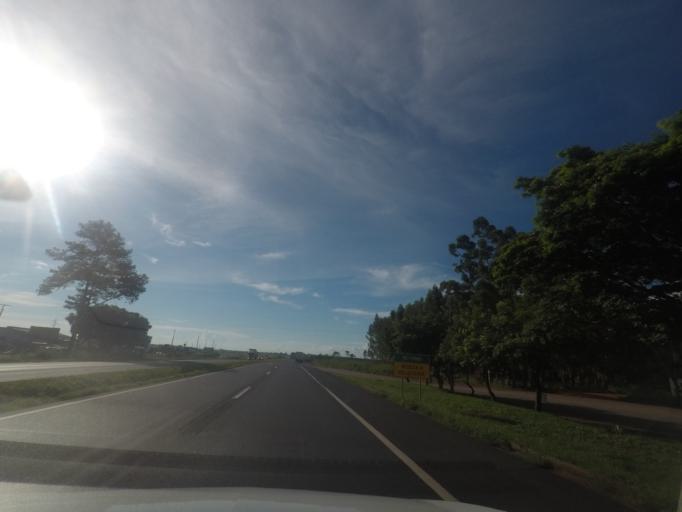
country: BR
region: Minas Gerais
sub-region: Centralina
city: Centralina
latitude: -18.7398
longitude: -49.0981
